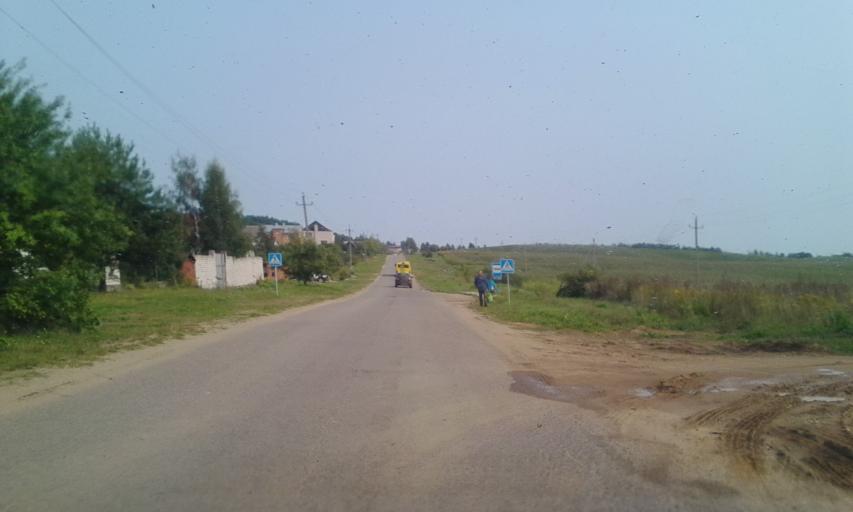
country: BY
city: Michanovichi
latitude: 53.7596
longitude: 27.6821
